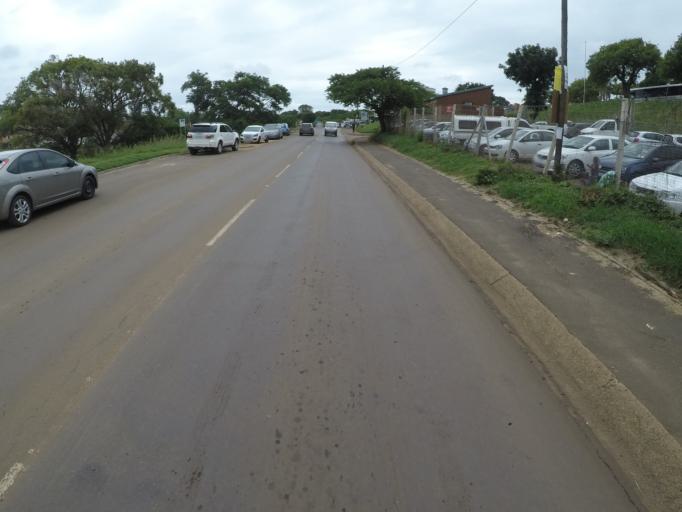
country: ZA
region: KwaZulu-Natal
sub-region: uThungulu District Municipality
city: Empangeni
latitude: -28.7784
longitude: 31.8641
